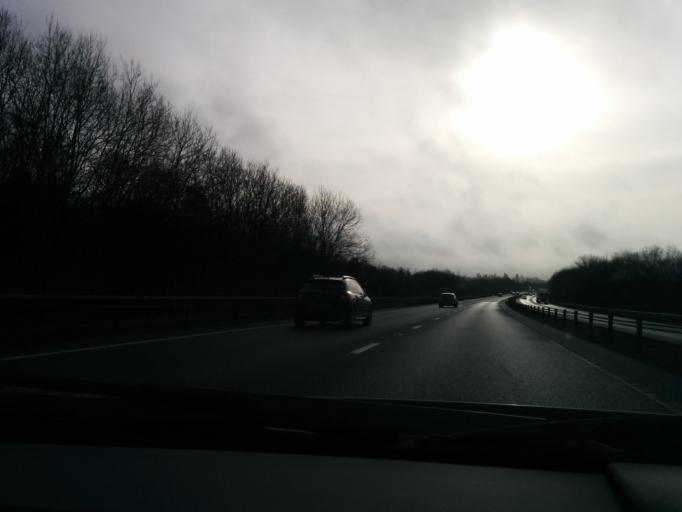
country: GB
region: England
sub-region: West Berkshire
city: Newbury
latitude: 51.4043
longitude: -1.3549
